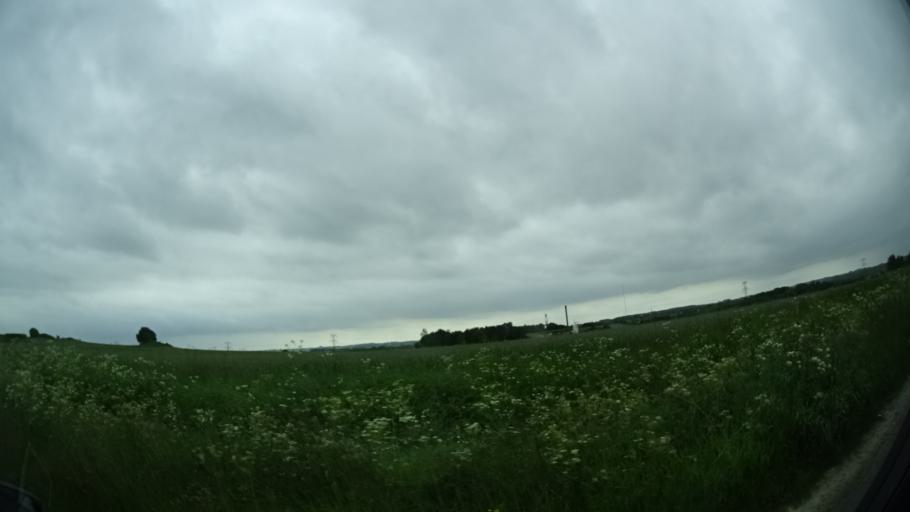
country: DK
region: Central Jutland
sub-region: Arhus Kommune
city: Kolt
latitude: 56.0990
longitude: 10.0664
